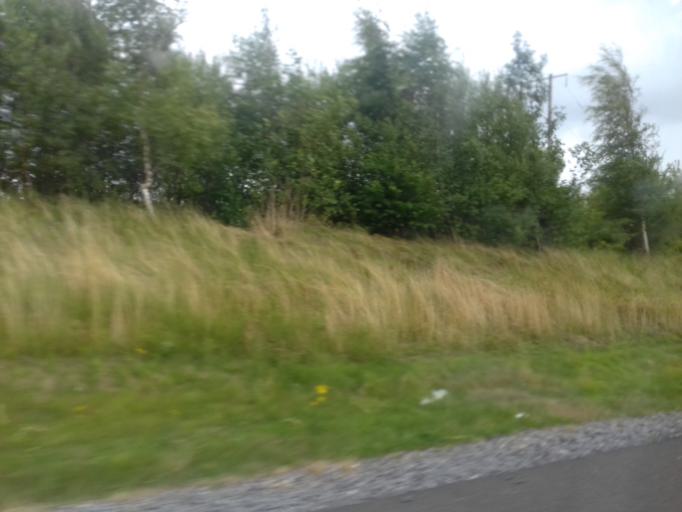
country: IE
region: Leinster
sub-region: Kilkenny
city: Thomastown
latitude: 52.6177
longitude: -7.1593
